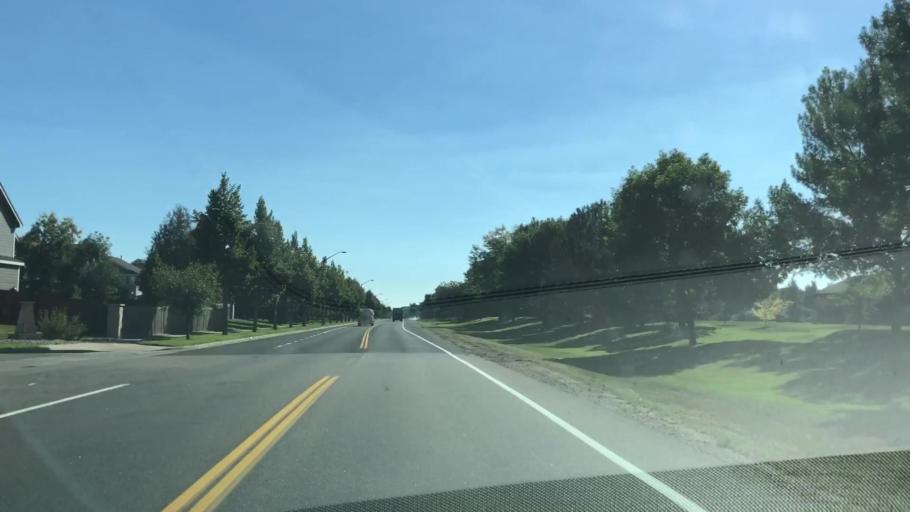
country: US
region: Colorado
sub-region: Larimer County
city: Fort Collins
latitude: 40.5091
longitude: -105.0293
